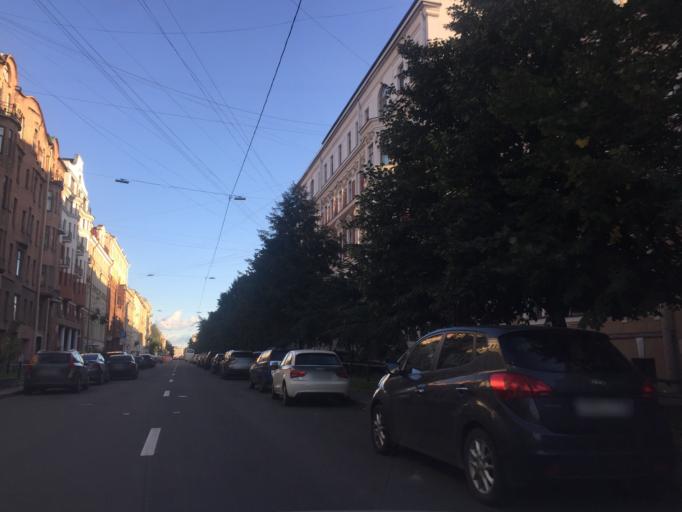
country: RU
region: St.-Petersburg
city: Saint Petersburg
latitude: 59.9434
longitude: 30.2851
